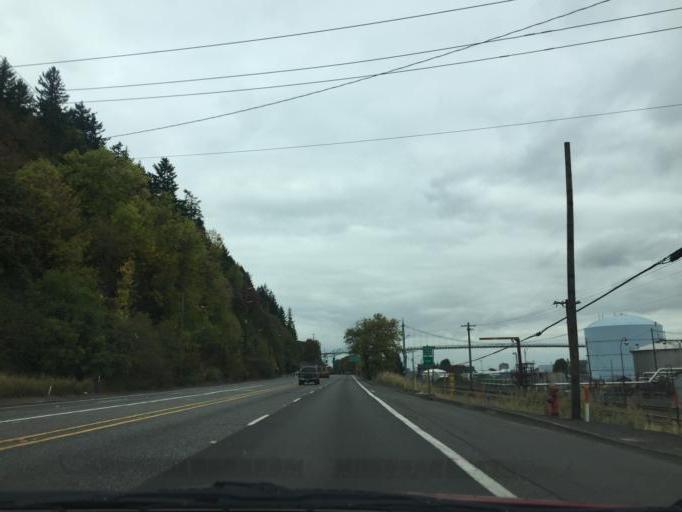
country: US
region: Oregon
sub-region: Washington County
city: West Haven
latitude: 45.5754
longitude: -122.7596
